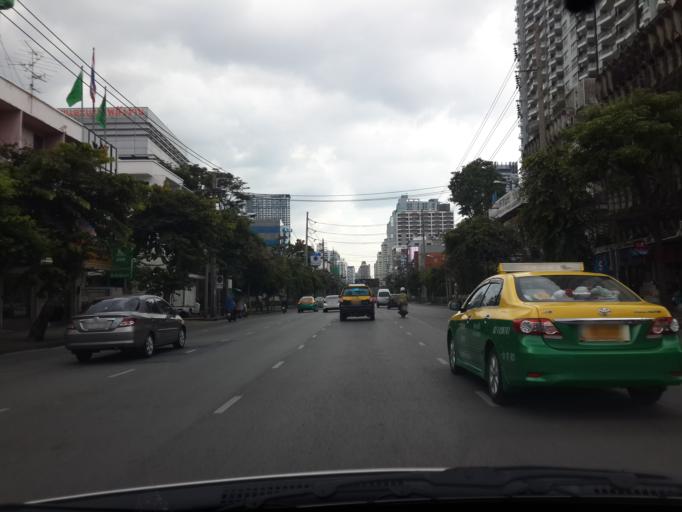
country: TH
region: Bangkok
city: Ratchathewi
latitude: 13.7556
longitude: 100.5251
